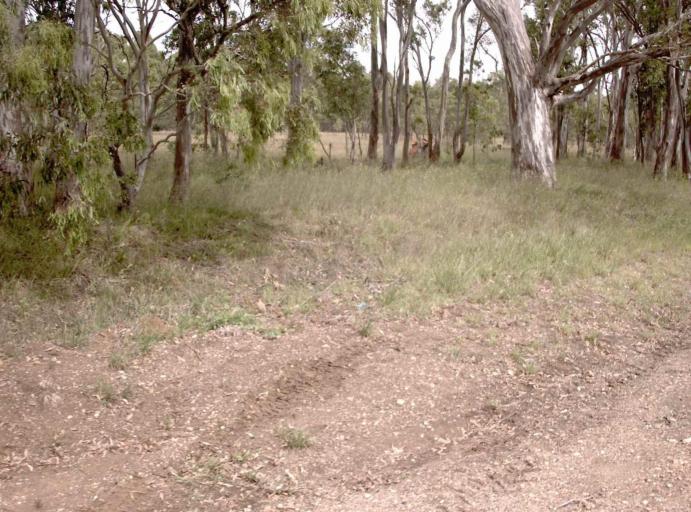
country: AU
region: Victoria
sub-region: Wellington
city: Sale
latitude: -37.9123
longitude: 147.0816
